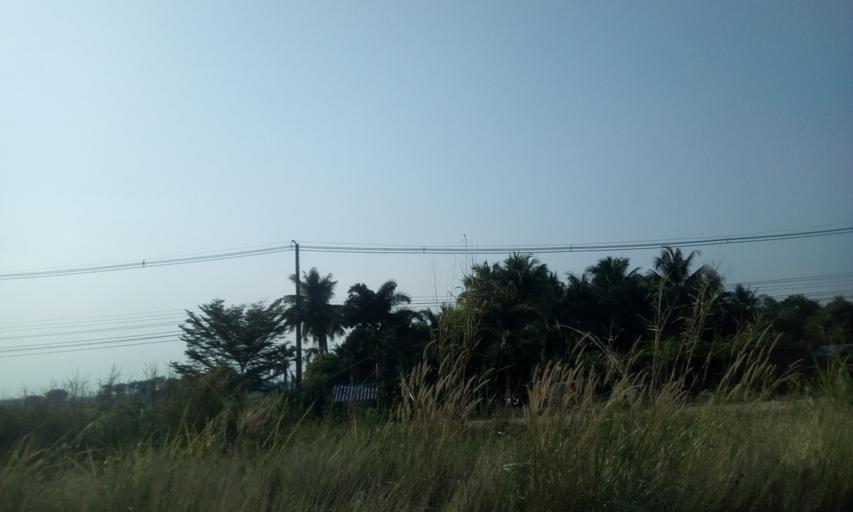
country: TH
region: Sing Buri
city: Phrom Buri
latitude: 14.8334
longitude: 100.4335
